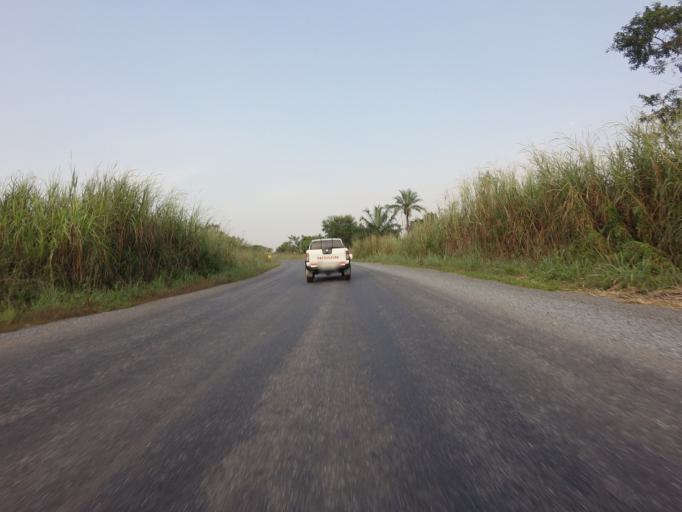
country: GH
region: Volta
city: Ho
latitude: 6.4608
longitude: 0.2197
